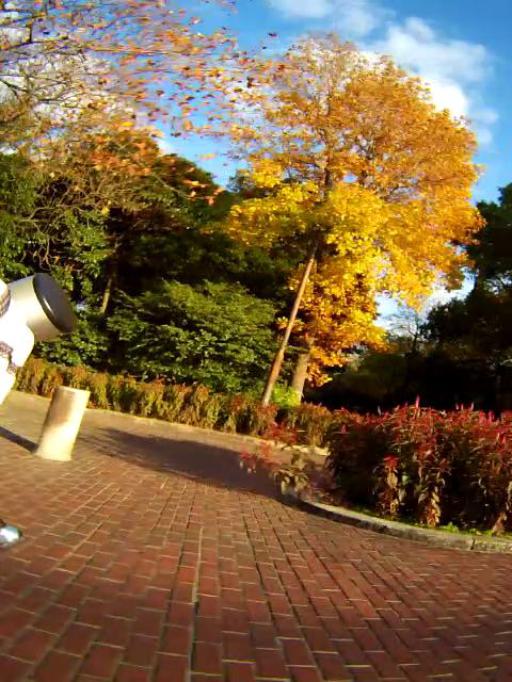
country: JP
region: Hyogo
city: Amagasaki
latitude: 34.7491
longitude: 135.4223
